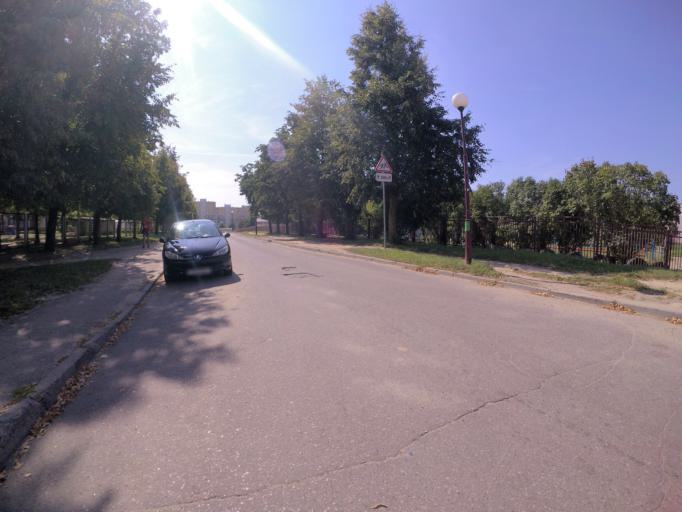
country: BY
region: Grodnenskaya
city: Hrodna
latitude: 53.7035
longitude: 23.8460
